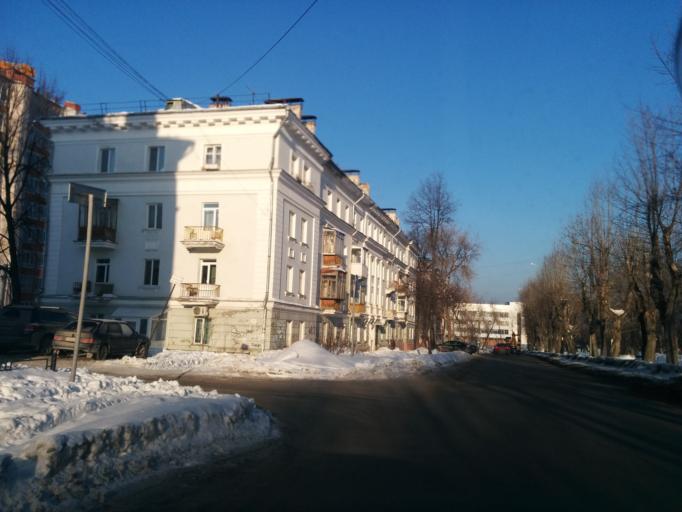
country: RU
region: Perm
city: Perm
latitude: 58.0202
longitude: 56.2859
